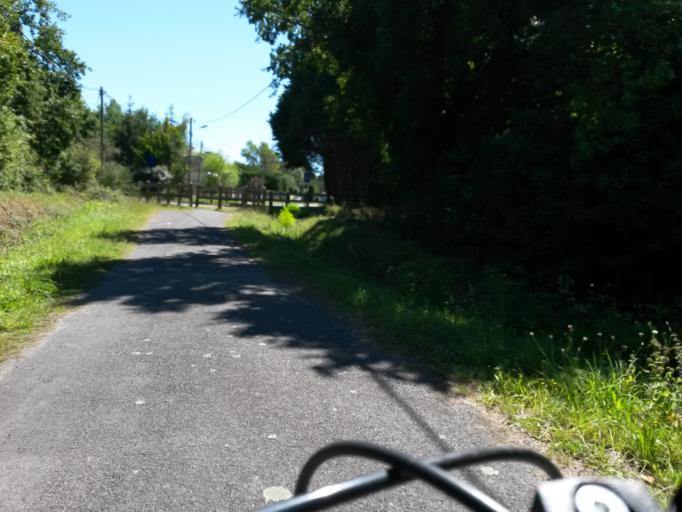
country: FR
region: Pays de la Loire
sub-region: Departement de la Loire-Atlantique
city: Mesquer
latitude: 47.4007
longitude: -2.4888
